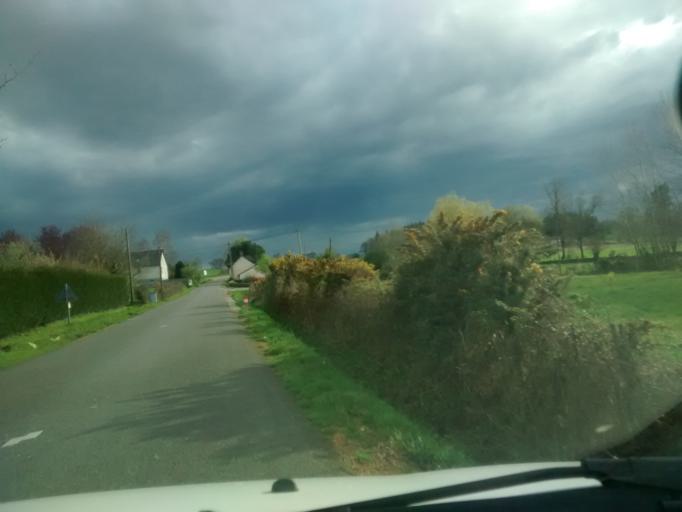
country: FR
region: Brittany
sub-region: Departement d'Ille-et-Vilaine
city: Servon-sur-Vilaine
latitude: 48.1579
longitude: -1.4909
